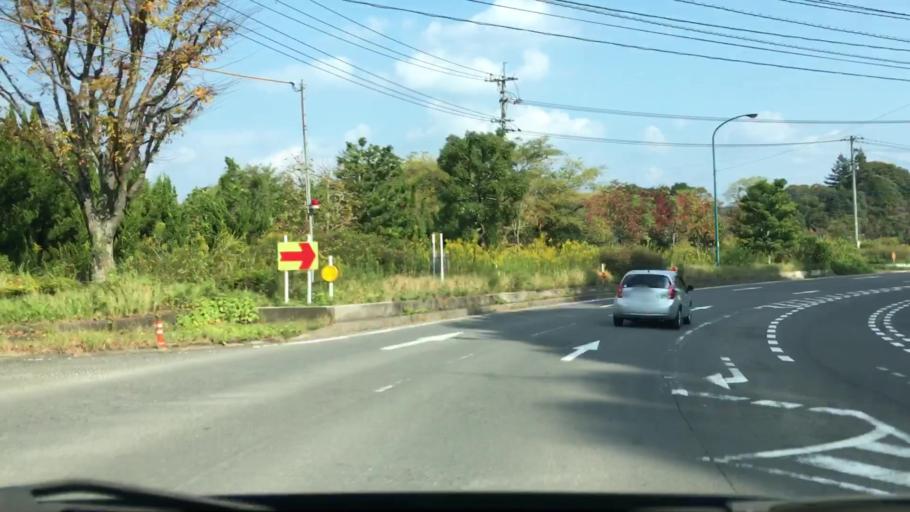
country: JP
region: Nagasaki
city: Sasebo
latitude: 32.9948
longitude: 129.7529
